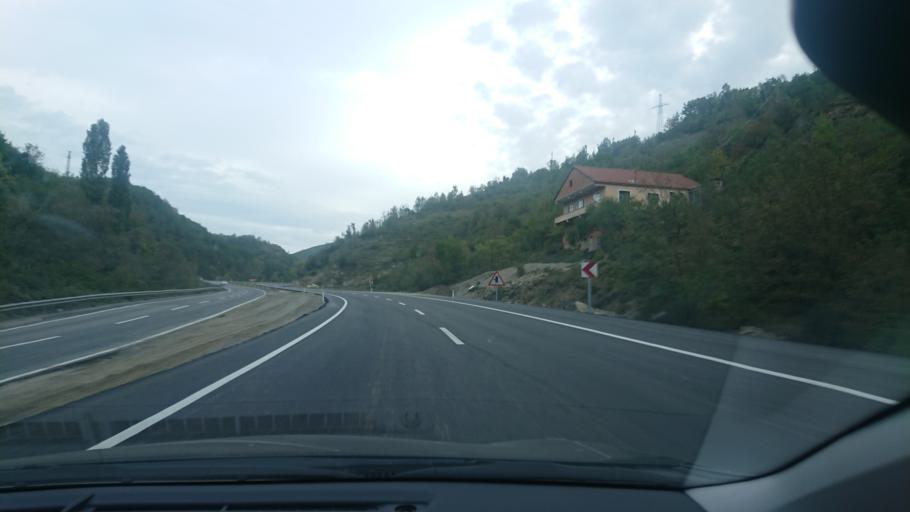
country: TR
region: Zonguldak
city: Beycuma
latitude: 41.3936
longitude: 31.9366
